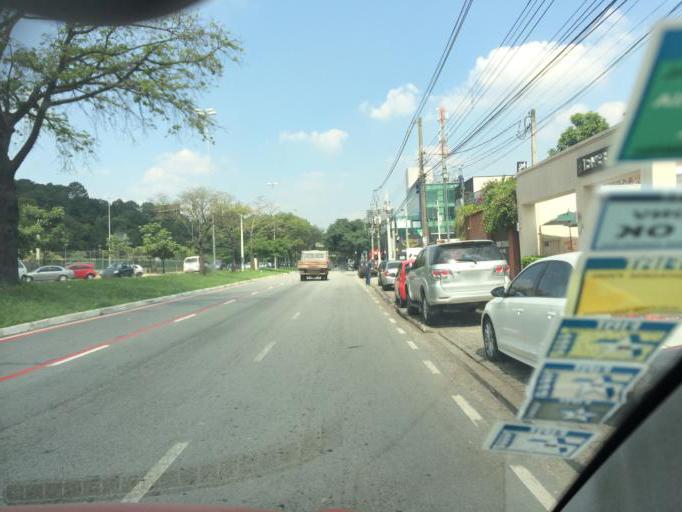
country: BR
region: Sao Paulo
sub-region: Guarulhos
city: Guarulhos
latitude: -23.4565
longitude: -46.5318
